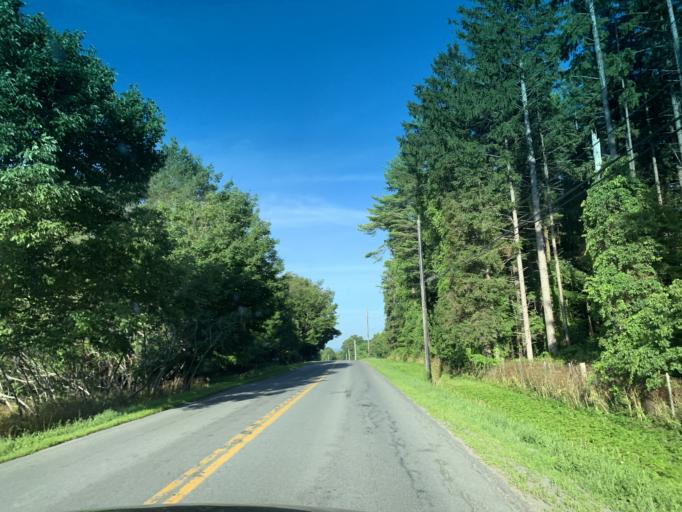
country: US
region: New York
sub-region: Oneida County
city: Clinton
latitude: 43.0547
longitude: -75.4439
